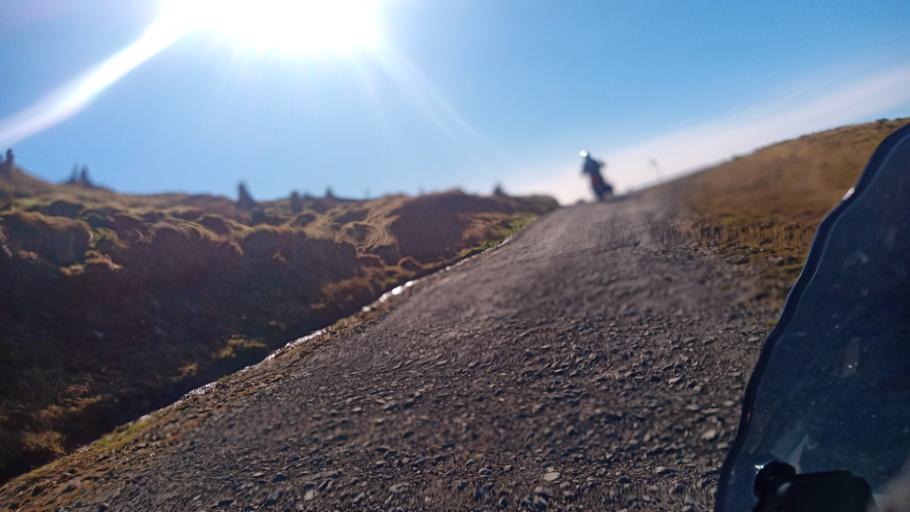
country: NZ
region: Gisborne
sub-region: Gisborne District
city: Gisborne
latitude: -38.1778
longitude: 177.8257
